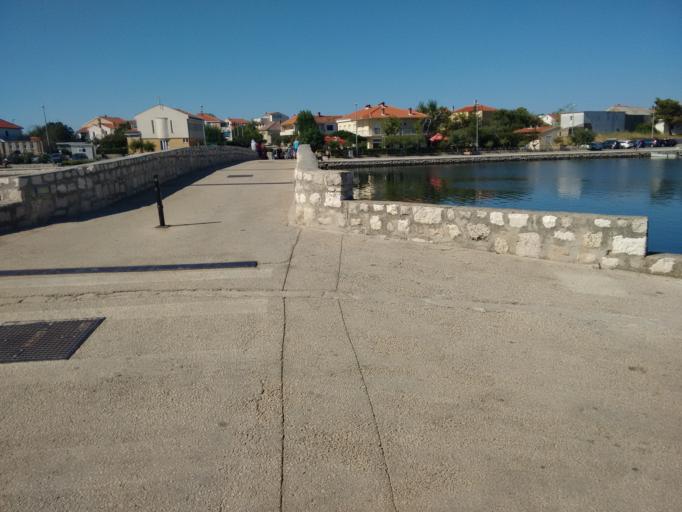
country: HR
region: Zadarska
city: Nin
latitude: 44.2415
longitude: 15.1819
